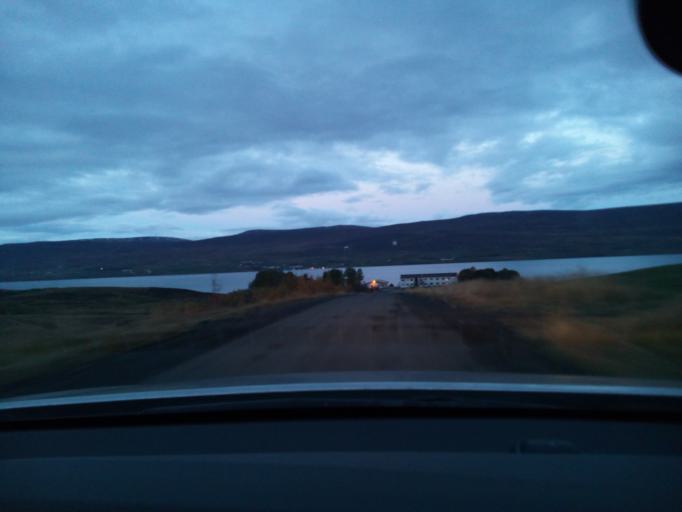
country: IS
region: Northeast
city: Akureyri
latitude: 65.7335
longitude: -18.1712
